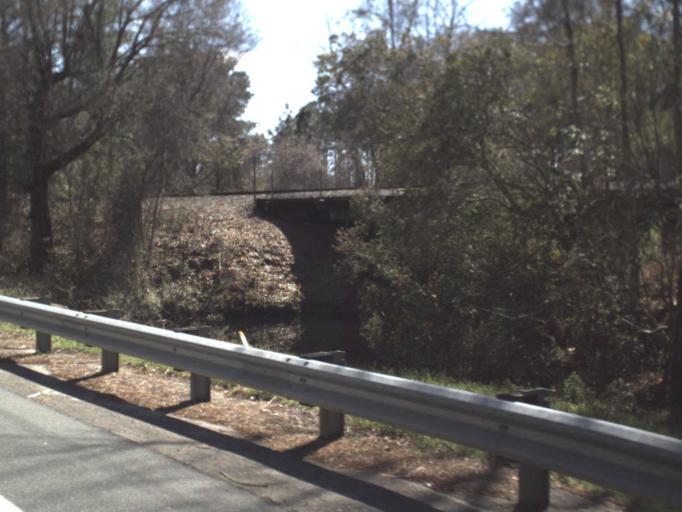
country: US
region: Florida
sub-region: Gadsden County
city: Gretna
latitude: 30.6290
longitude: -84.6702
